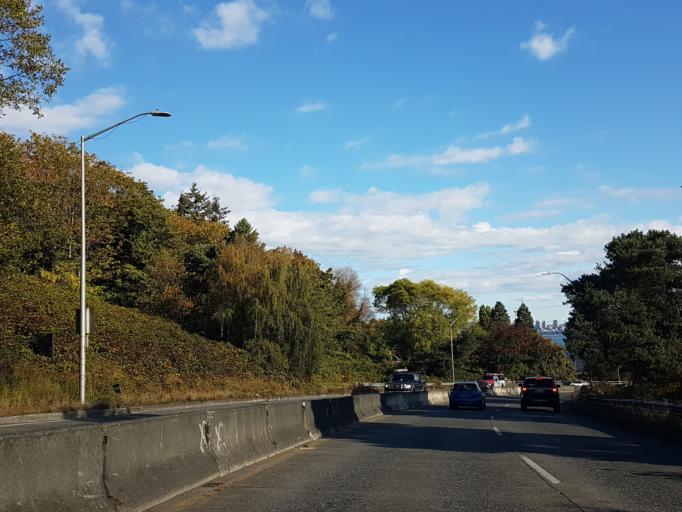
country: US
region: Washington
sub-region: King County
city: Seattle
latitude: 47.5698
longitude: -122.3728
